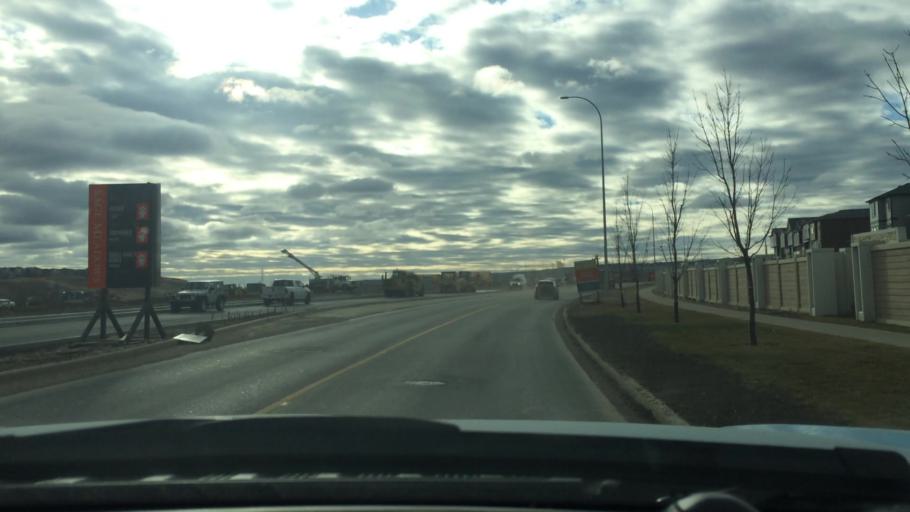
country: CA
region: Alberta
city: Calgary
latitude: 51.1795
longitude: -114.1336
